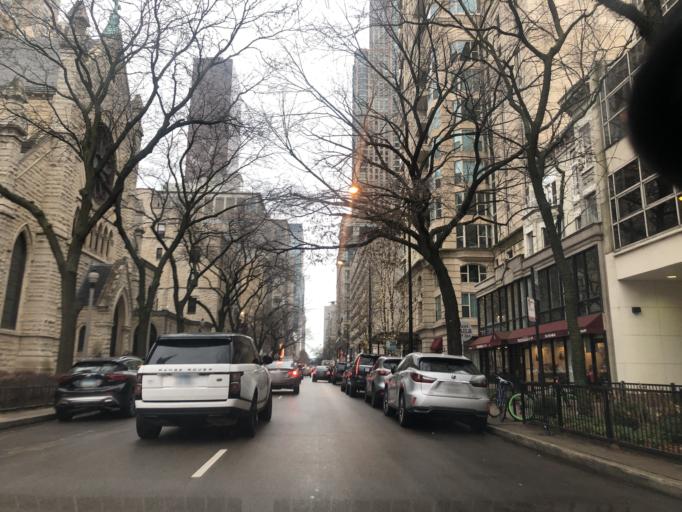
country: US
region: Illinois
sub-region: Cook County
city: Chicago
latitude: 41.8957
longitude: -87.6280
